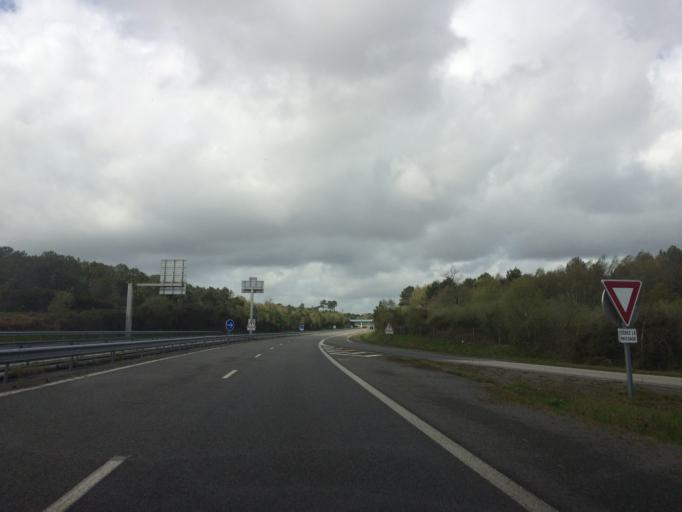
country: FR
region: Brittany
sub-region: Departement du Morbihan
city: Pluherlin
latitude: 47.6697
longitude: -2.3582
